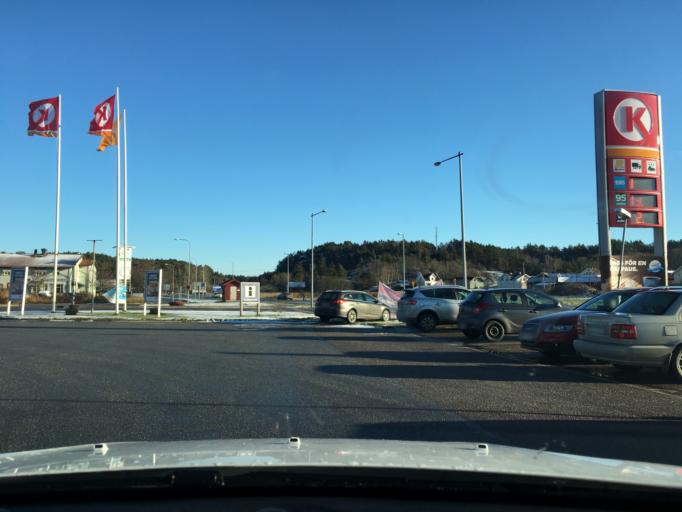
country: SE
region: Vaestra Goetaland
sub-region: Tjorns Kommun
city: Myggenas
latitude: 58.0240
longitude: 11.6560
